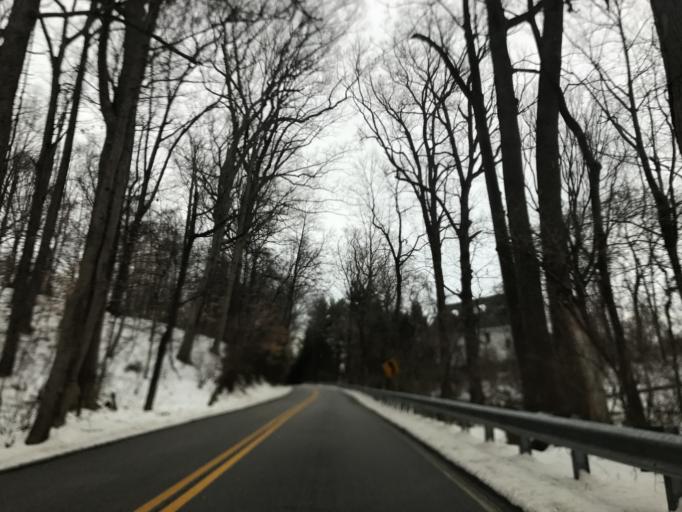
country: US
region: Maryland
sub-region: Baltimore County
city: Mays Chapel
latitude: 39.4326
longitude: -76.6645
